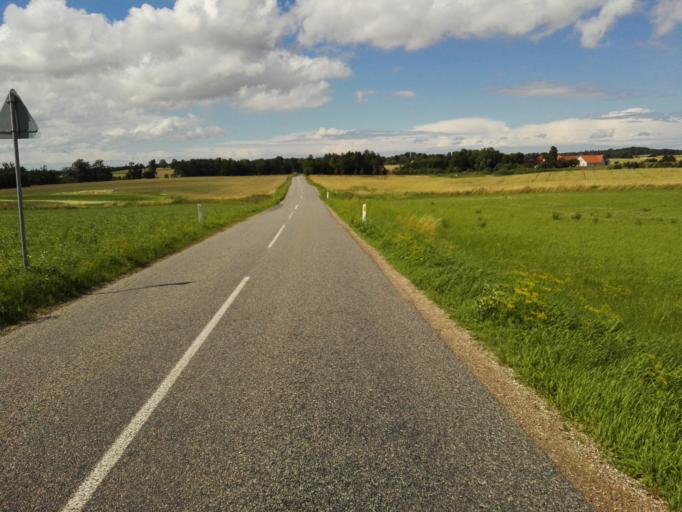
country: DK
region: Capital Region
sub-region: Egedal Kommune
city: Ganlose
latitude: 55.7891
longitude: 12.2340
